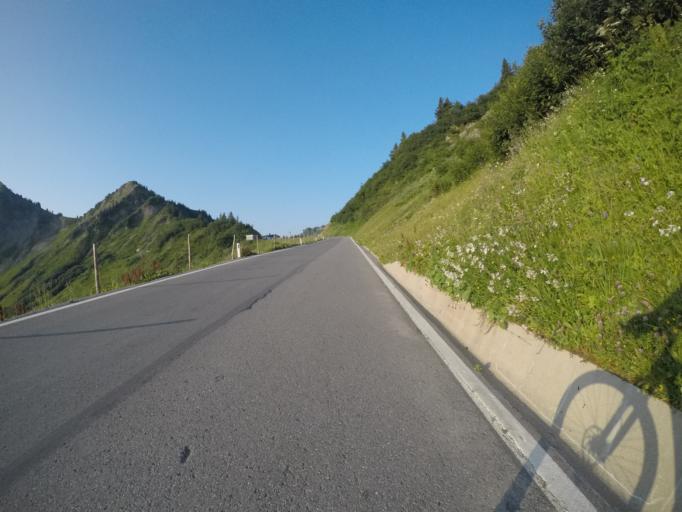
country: AT
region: Vorarlberg
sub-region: Politischer Bezirk Bludenz
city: Blons
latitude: 47.2678
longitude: 9.8333
